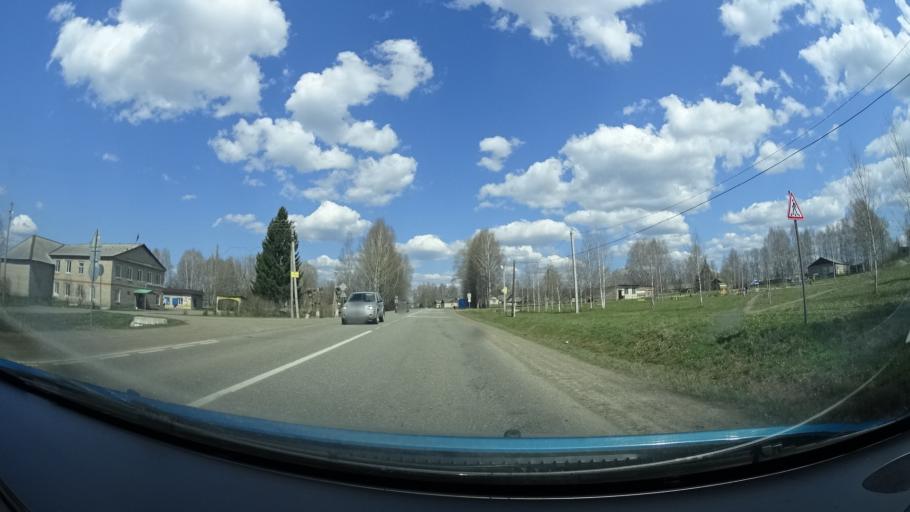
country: RU
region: Perm
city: Osa
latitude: 57.3695
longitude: 55.6075
